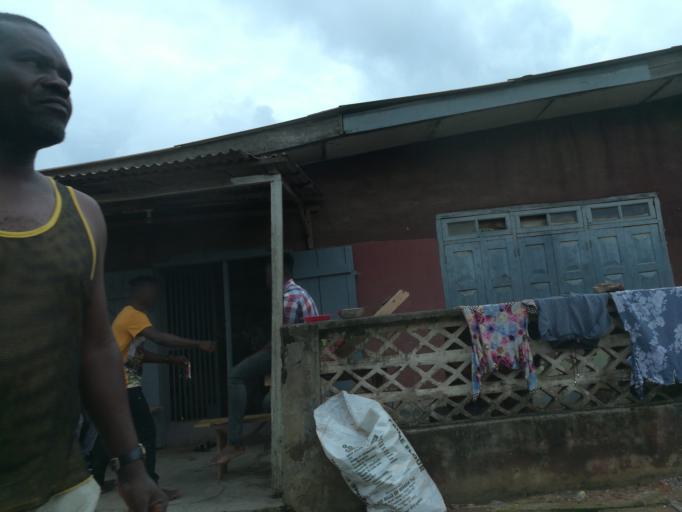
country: NG
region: Lagos
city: Agege
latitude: 6.6140
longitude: 3.3114
